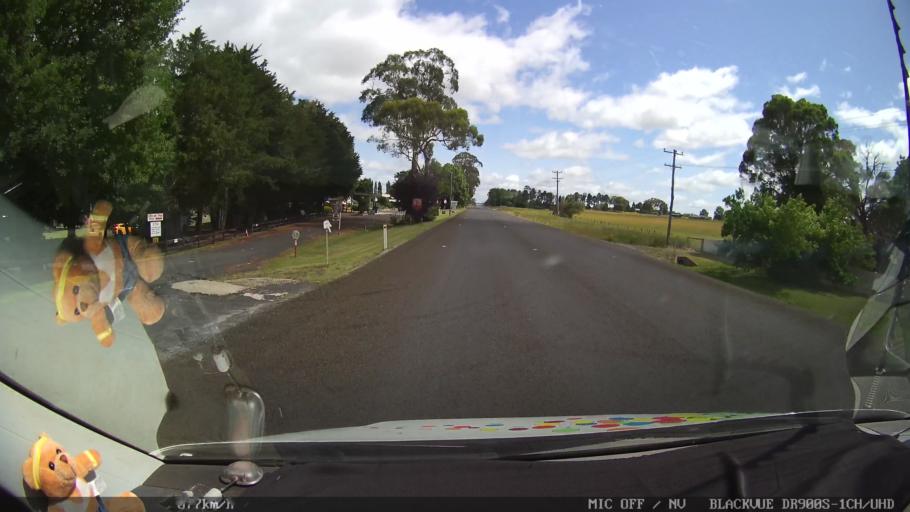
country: AU
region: New South Wales
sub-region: Glen Innes Severn
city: Glen Innes
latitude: -29.7720
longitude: 151.7318
